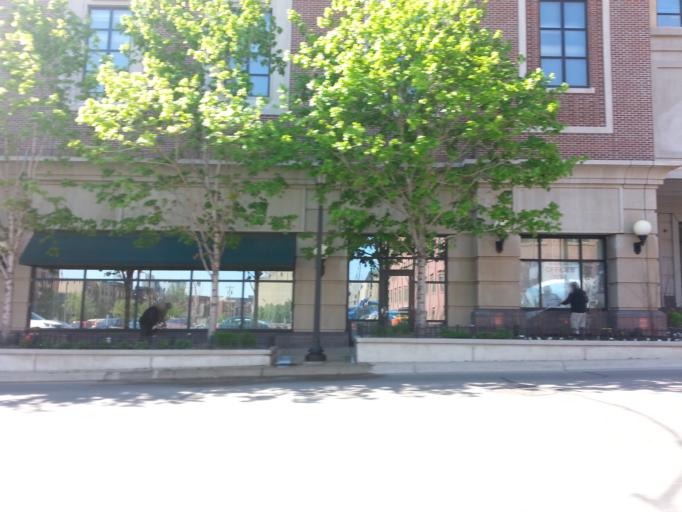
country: US
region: Minnesota
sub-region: Hennepin County
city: Minneapolis
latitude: 44.9813
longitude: -93.2629
